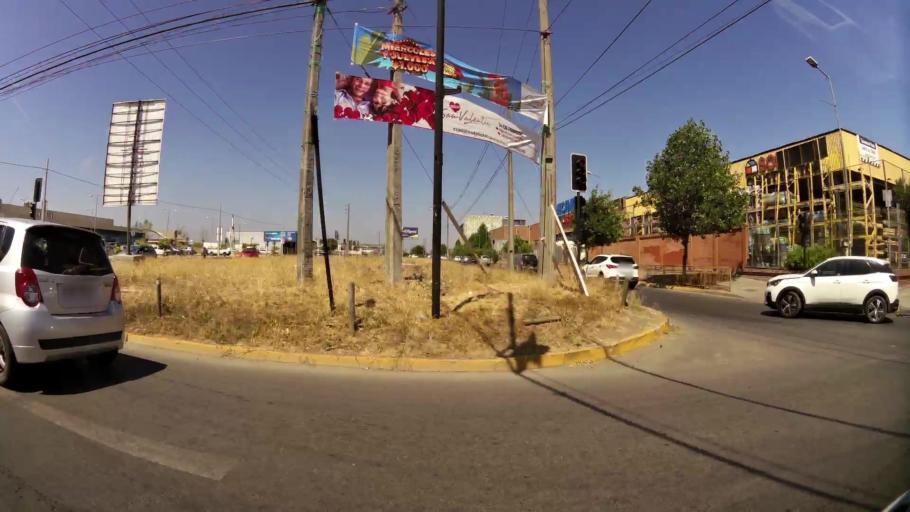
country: CL
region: Maule
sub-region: Provincia de Talca
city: Talca
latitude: -35.4314
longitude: -71.6281
